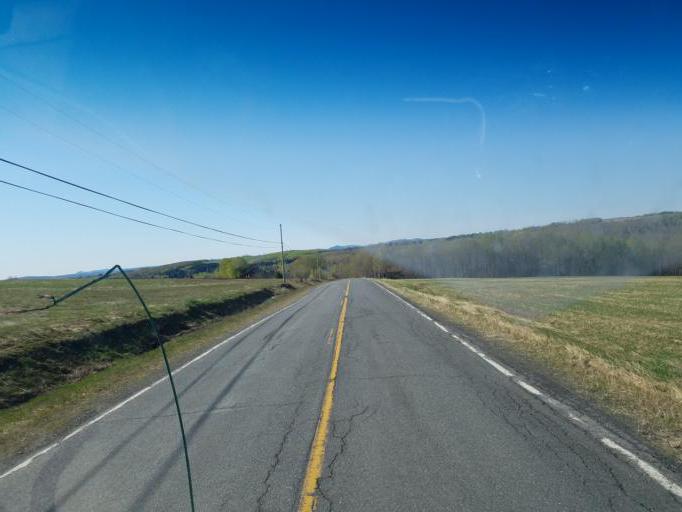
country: US
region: Maine
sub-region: Aroostook County
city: Caribou
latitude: 46.8617
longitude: -68.2085
